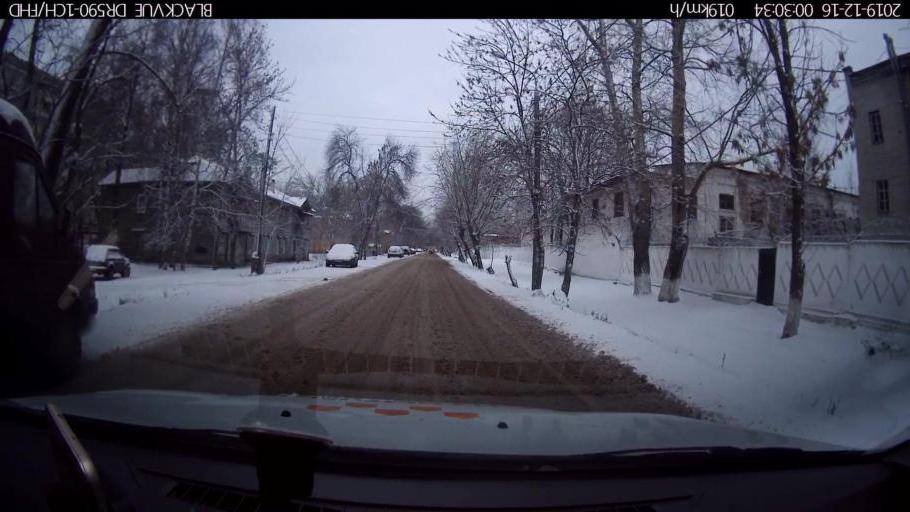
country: RU
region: Nizjnij Novgorod
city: Nizhniy Novgorod
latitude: 56.3103
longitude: 43.8906
